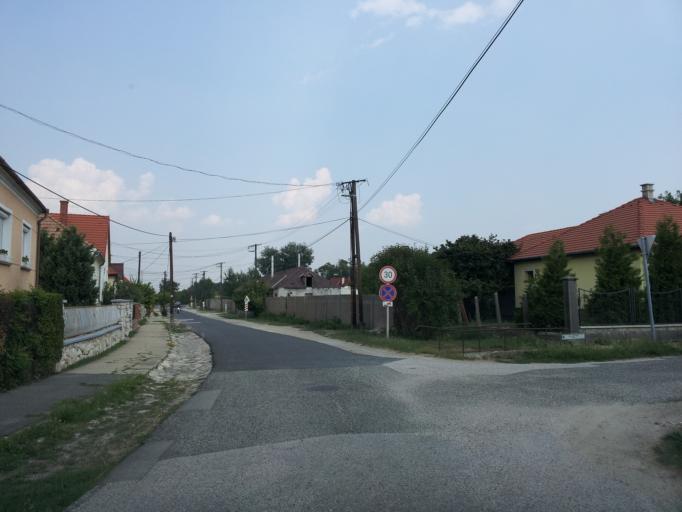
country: HU
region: Gyor-Moson-Sopron
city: Nyul
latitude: 47.5872
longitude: 17.6953
